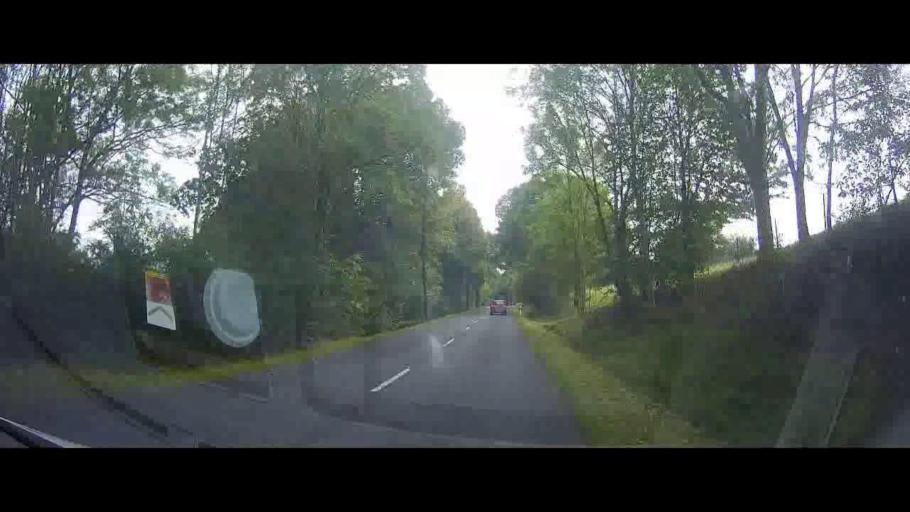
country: DE
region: Lower Saxony
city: Rosdorf
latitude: 51.5523
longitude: 9.8623
